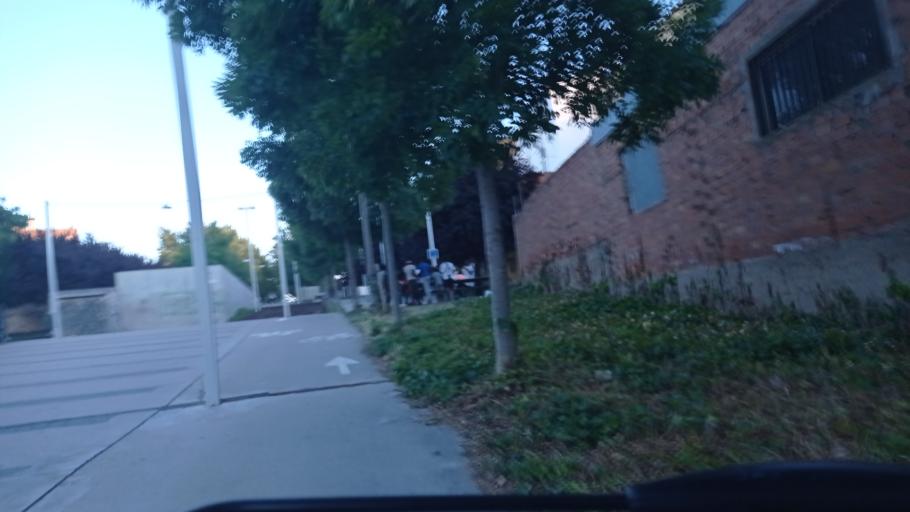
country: ES
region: Aragon
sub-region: Provincia de Zaragoza
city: Oliver-Valdefierro, Oliver, Valdefierro
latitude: 41.6526
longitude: -0.9245
